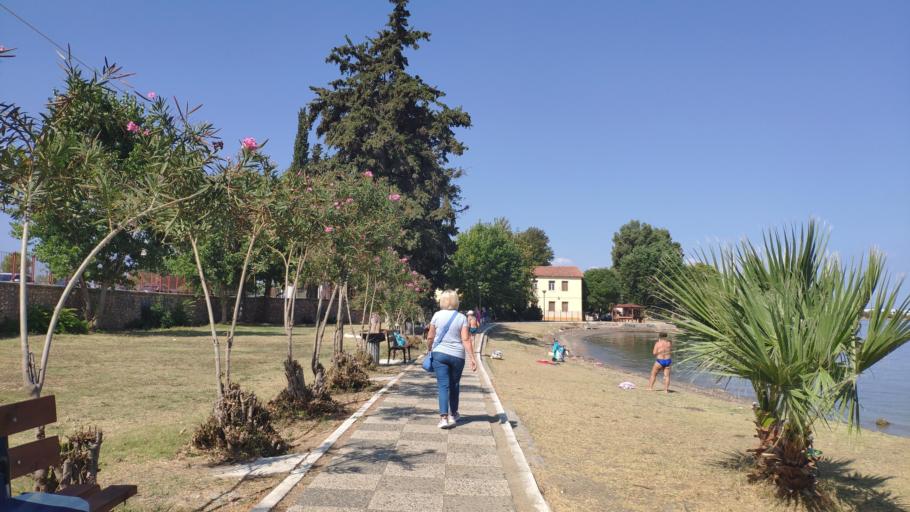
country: GR
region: Attica
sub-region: Nomarchia Anatolikis Attikis
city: Skala Oropou
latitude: 38.3213
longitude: 23.7875
